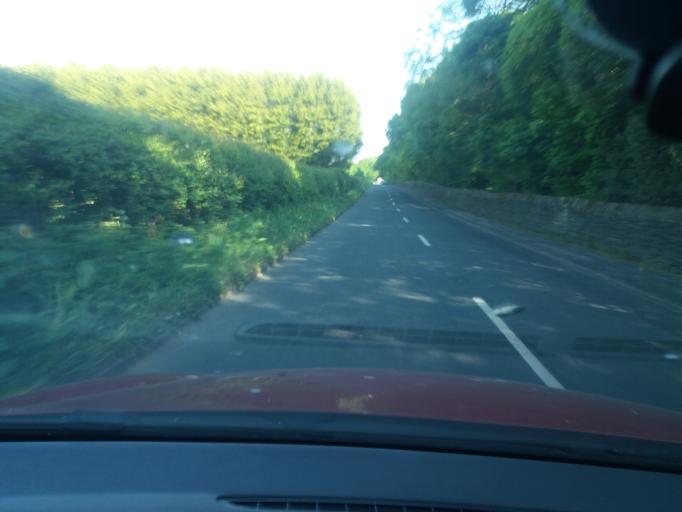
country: GB
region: England
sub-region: Borough of Wigan
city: Haigh
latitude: 53.6182
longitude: -2.5808
